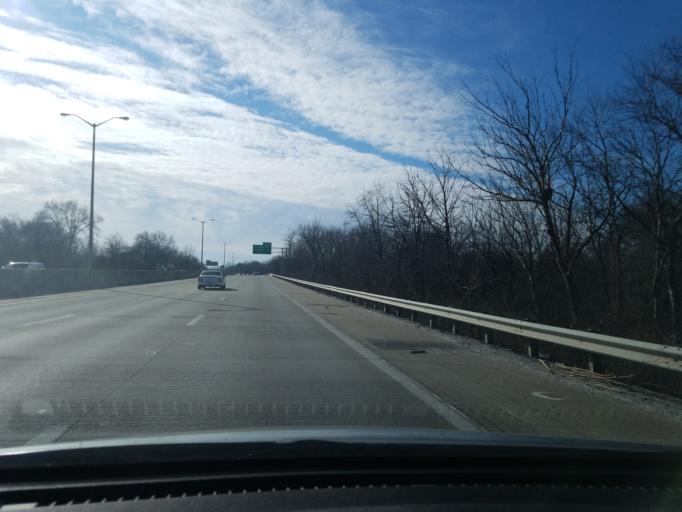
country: US
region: Indiana
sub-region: Floyd County
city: New Albany
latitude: 38.2472
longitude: -85.8094
